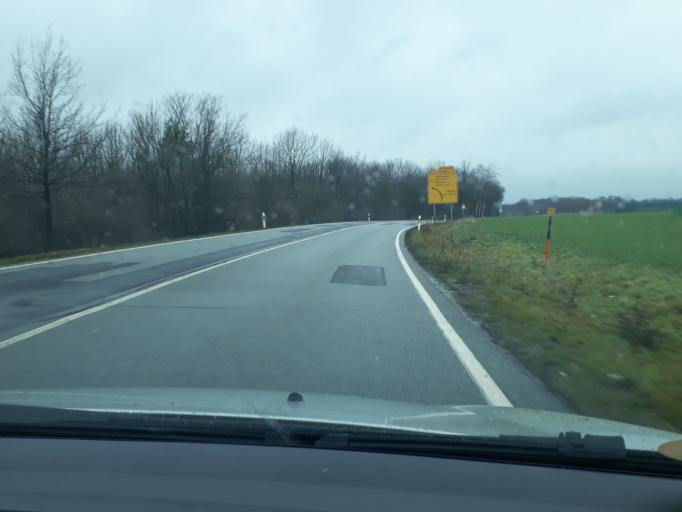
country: DE
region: Saxony
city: Grossdubrau
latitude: 51.2094
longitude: 14.4723
